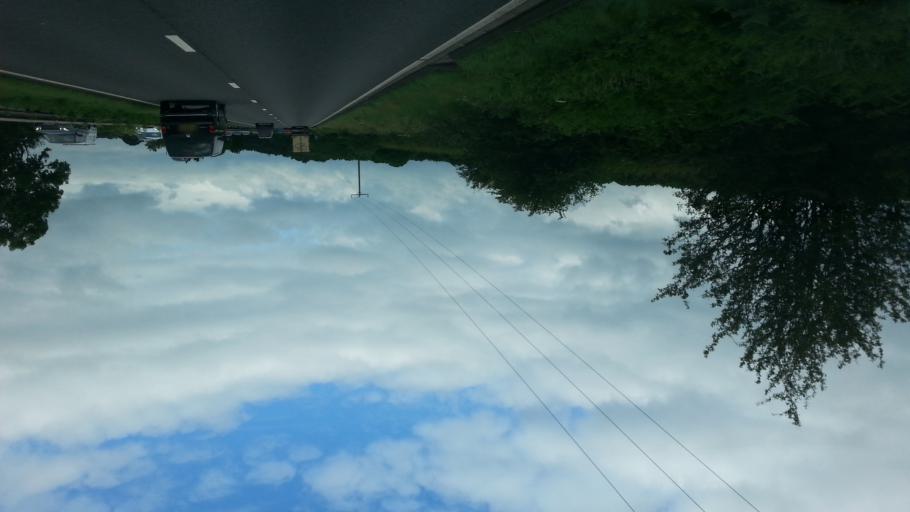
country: GB
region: England
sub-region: Nottinghamshire
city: Babworth
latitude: 53.2892
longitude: -1.0149
